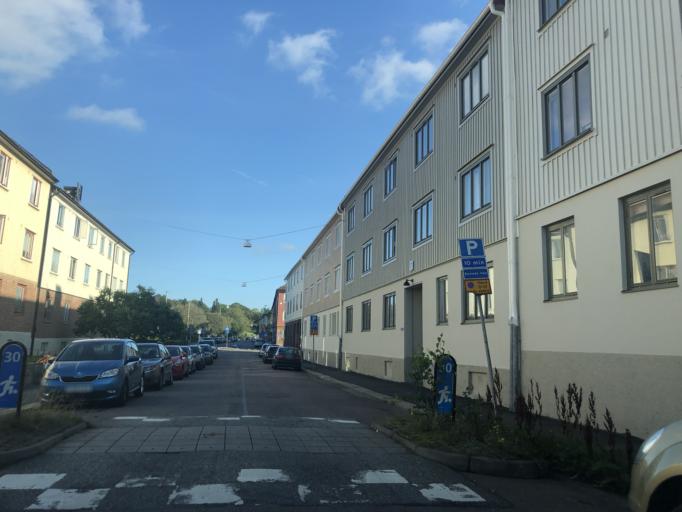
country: SE
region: Vaestra Goetaland
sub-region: Goteborg
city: Majorna
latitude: 57.6864
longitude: 11.9263
